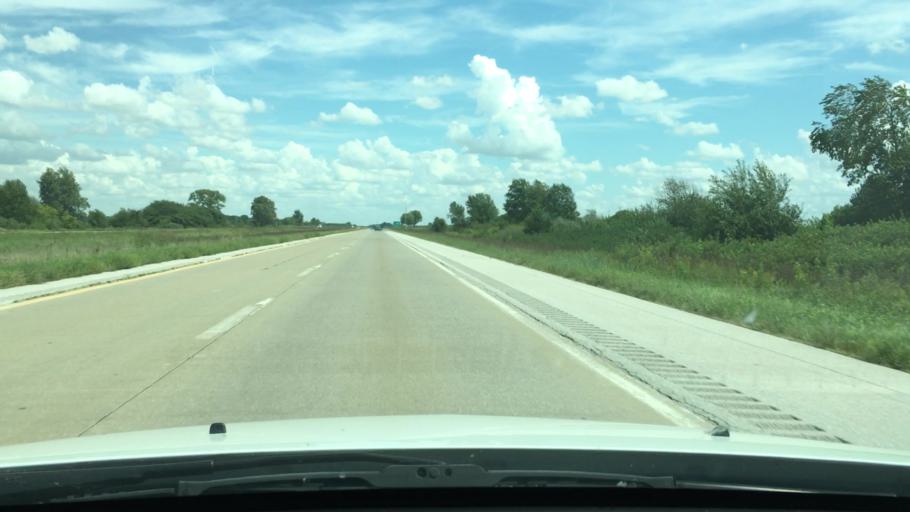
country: US
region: Illinois
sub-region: Scott County
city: Winchester
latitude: 39.6809
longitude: -90.4883
